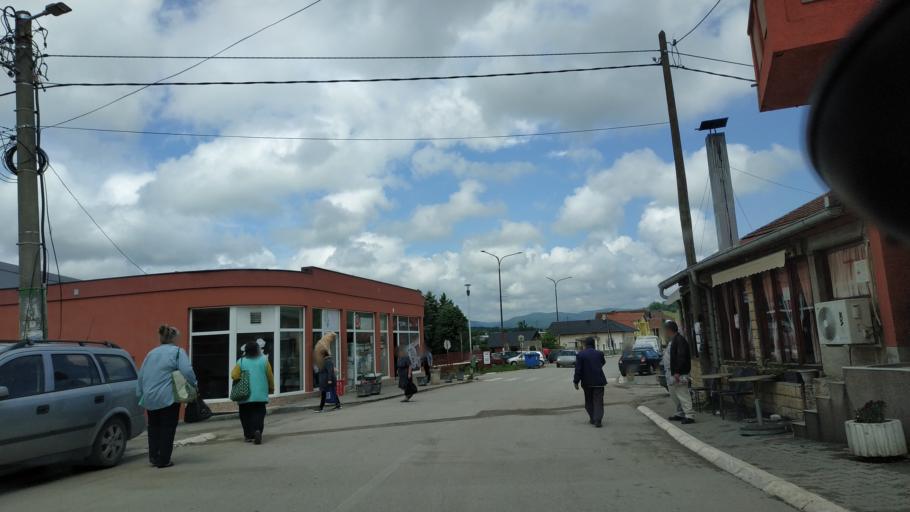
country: RS
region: Central Serbia
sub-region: Zajecarski Okrug
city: Boljevac
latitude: 43.8314
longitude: 21.9600
